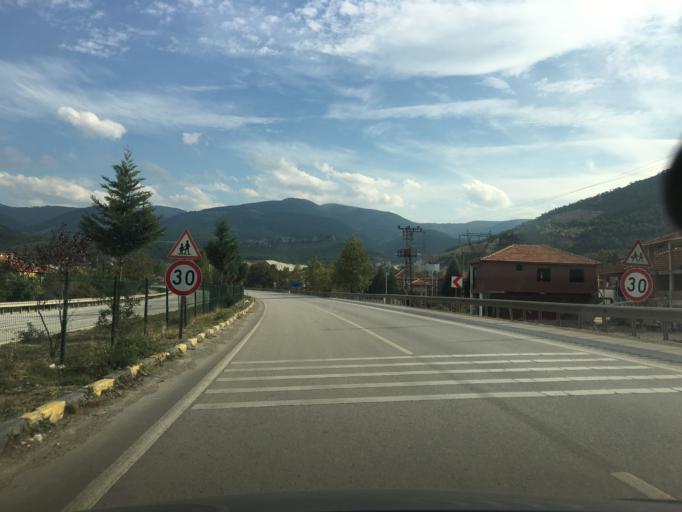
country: TR
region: Karabuk
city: Karabuk
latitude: 41.1026
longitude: 32.6693
